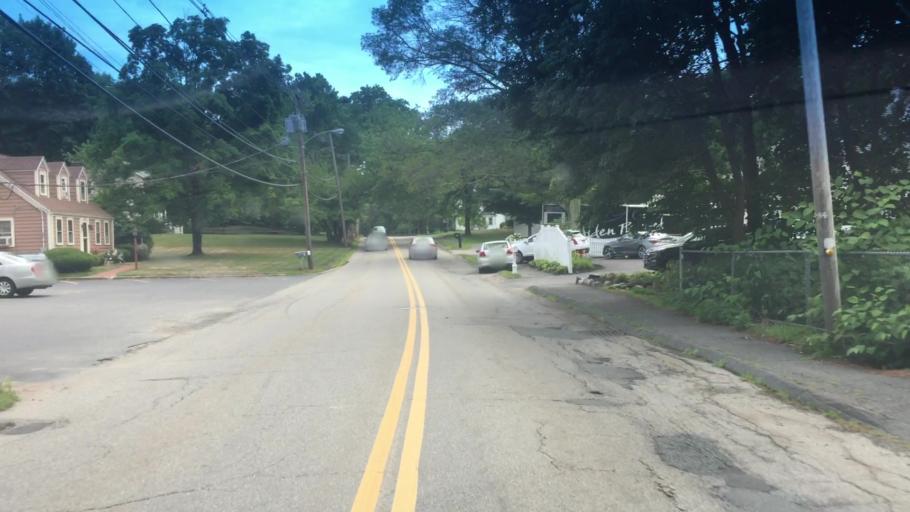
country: US
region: Massachusetts
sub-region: Norfolk County
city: Franklin
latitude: 42.1032
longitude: -71.3960
